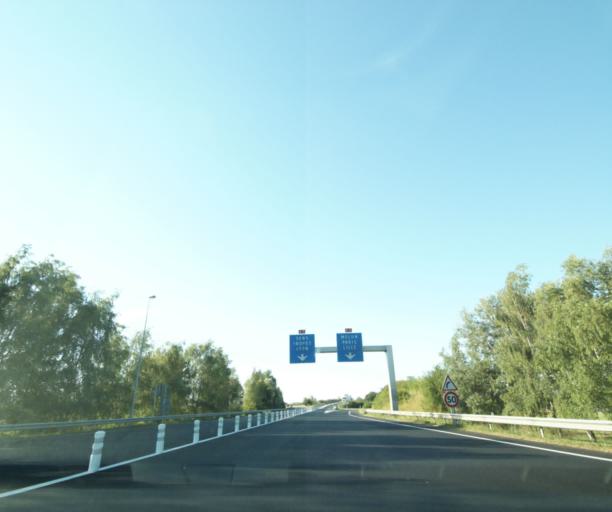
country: FR
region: Ile-de-France
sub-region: Departement de Seine-et-Marne
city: Marolles-sur-Seine
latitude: 48.3795
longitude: 3.0206
